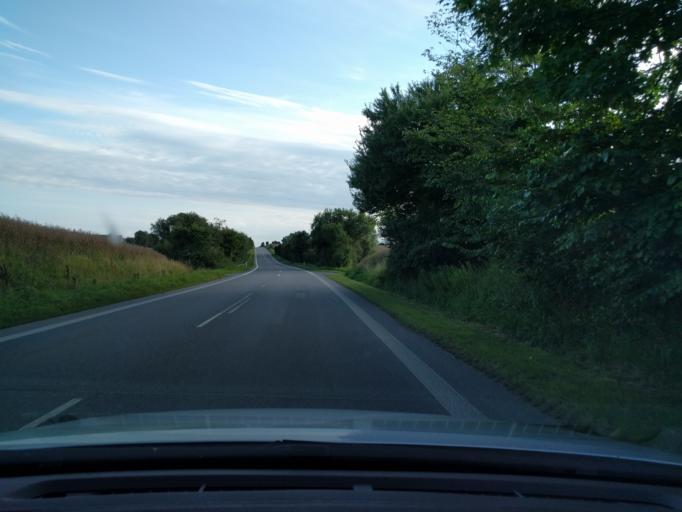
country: DK
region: Zealand
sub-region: Guldborgsund Kommune
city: Stubbekobing
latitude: 54.8784
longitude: 12.0292
